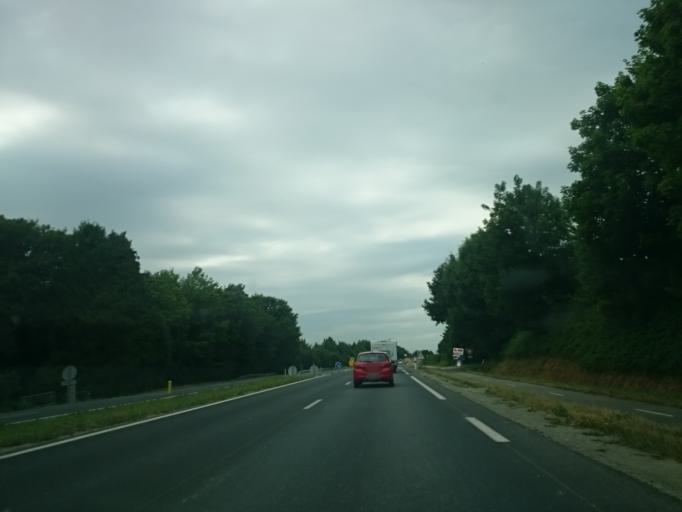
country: FR
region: Brittany
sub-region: Departement du Finistere
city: Guilers
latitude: 48.4124
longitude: -4.5400
